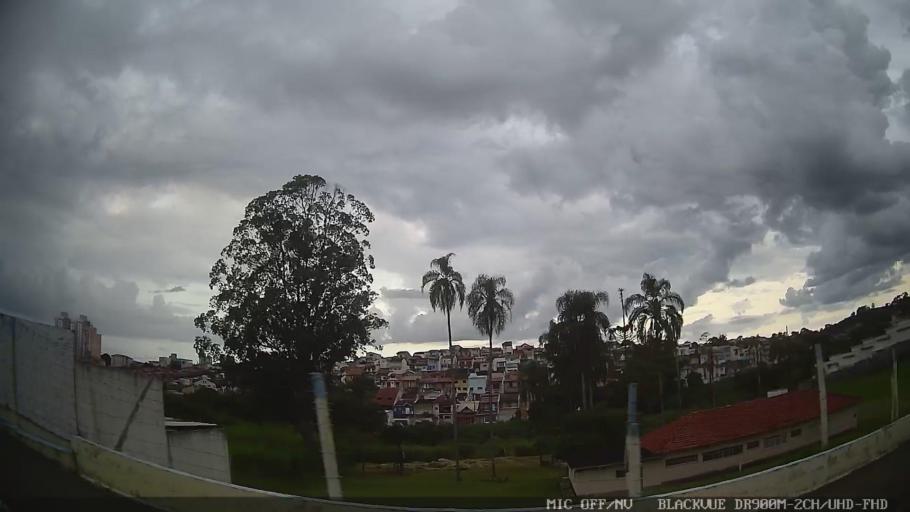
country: BR
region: Sao Paulo
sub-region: Mogi das Cruzes
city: Mogi das Cruzes
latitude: -23.5451
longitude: -46.1983
